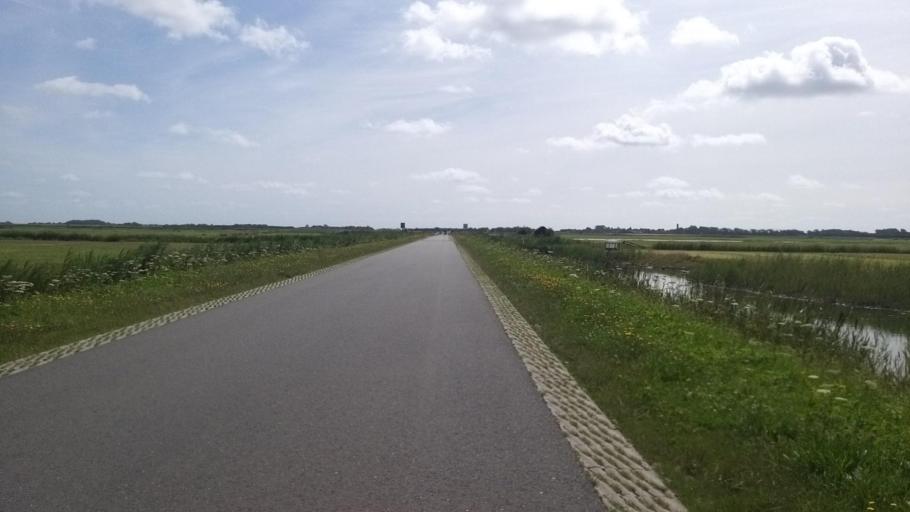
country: NL
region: North Holland
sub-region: Gemeente Texel
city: Den Burg
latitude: 53.0836
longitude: 4.7978
